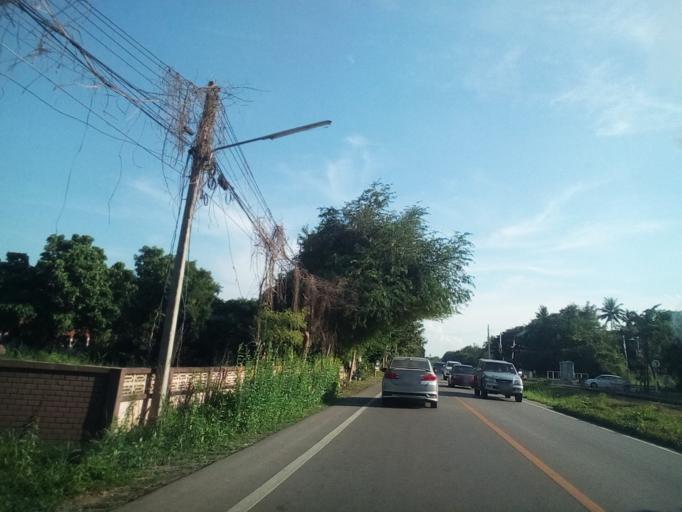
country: TH
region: Chiang Mai
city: Saraphi
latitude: 18.7083
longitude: 99.0428
